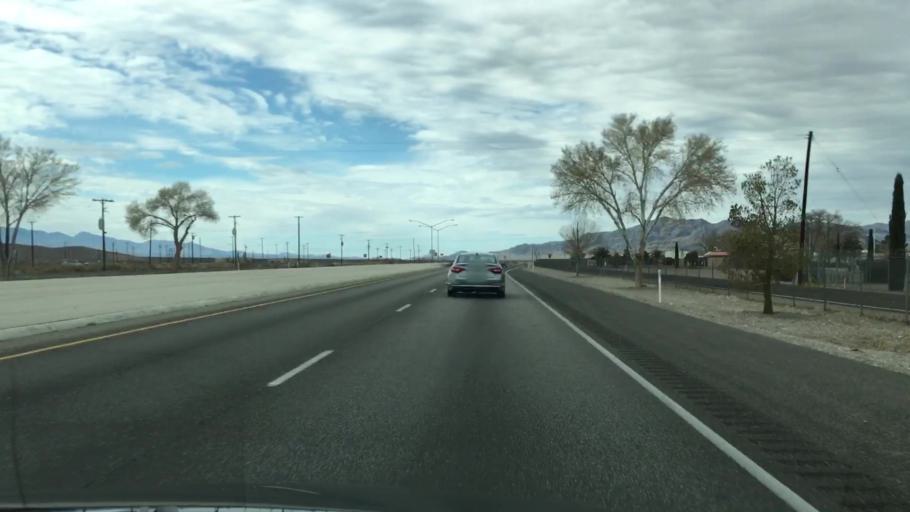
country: US
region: Nevada
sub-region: Nye County
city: Pahrump
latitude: 36.5778
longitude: -115.6747
